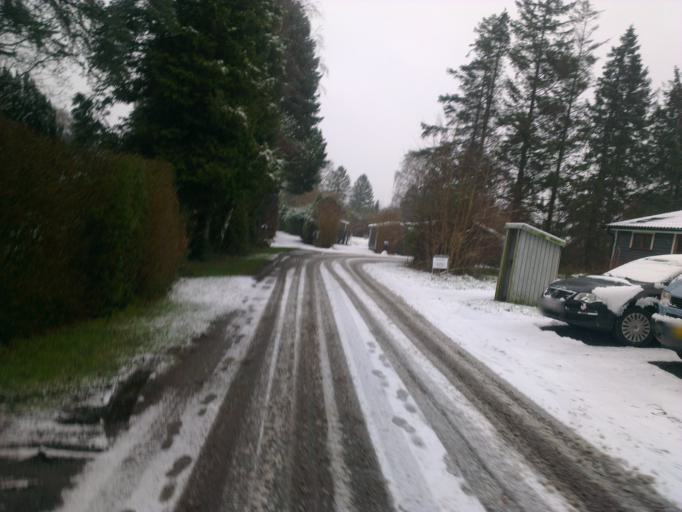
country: DK
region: Capital Region
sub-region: Frederikssund Kommune
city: Jaegerspris
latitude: 55.8355
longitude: 11.9651
